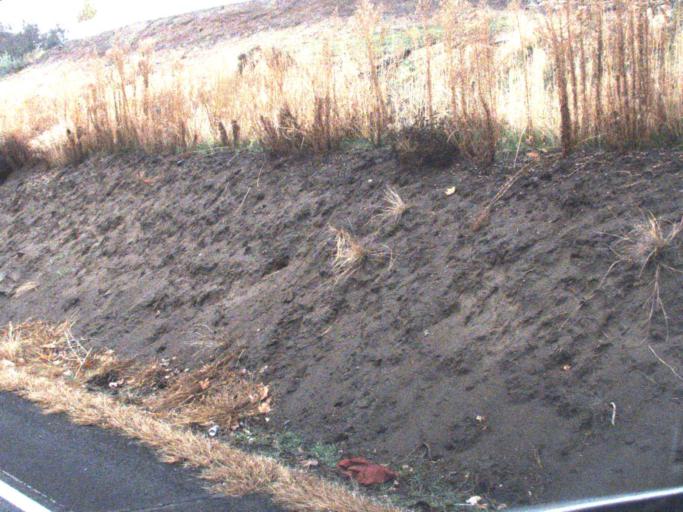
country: US
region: Washington
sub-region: Asotin County
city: West Clarkston-Highland
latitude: 46.3771
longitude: -117.0539
